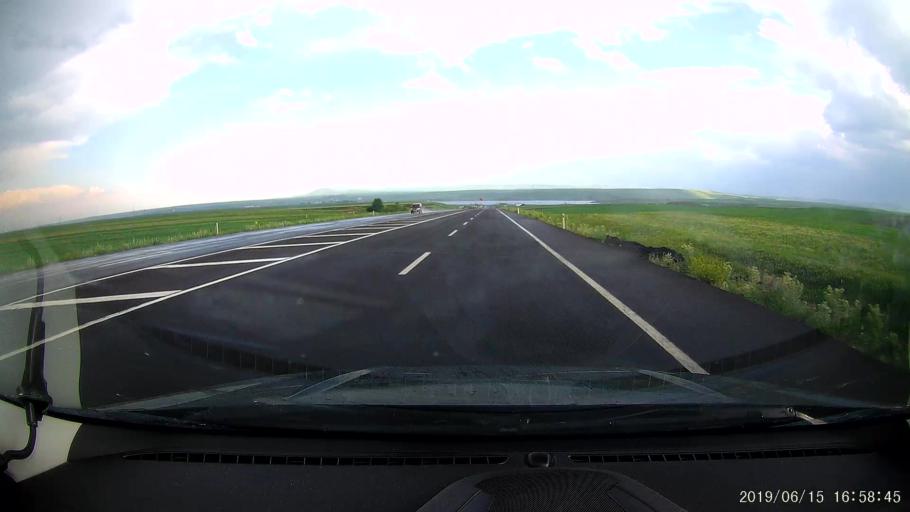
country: TR
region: Kars
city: Susuz
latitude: 40.7609
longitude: 43.1457
